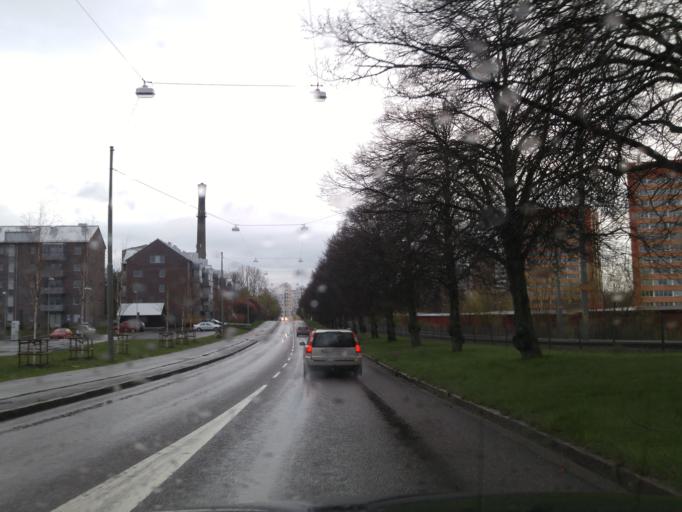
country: SE
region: Vaestra Goetaland
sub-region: Goteborg
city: Majorna
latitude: 57.6587
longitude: 11.9202
